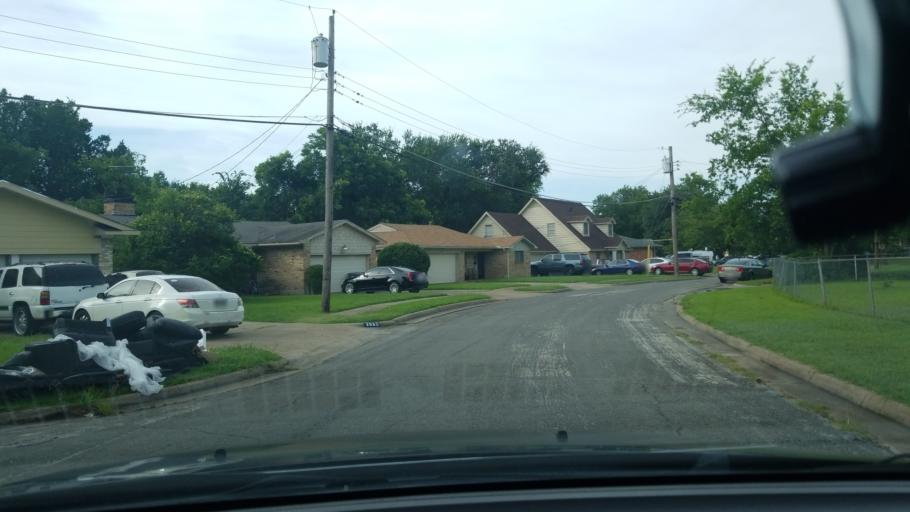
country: US
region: Texas
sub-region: Dallas County
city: Balch Springs
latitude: 32.7582
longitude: -96.6643
